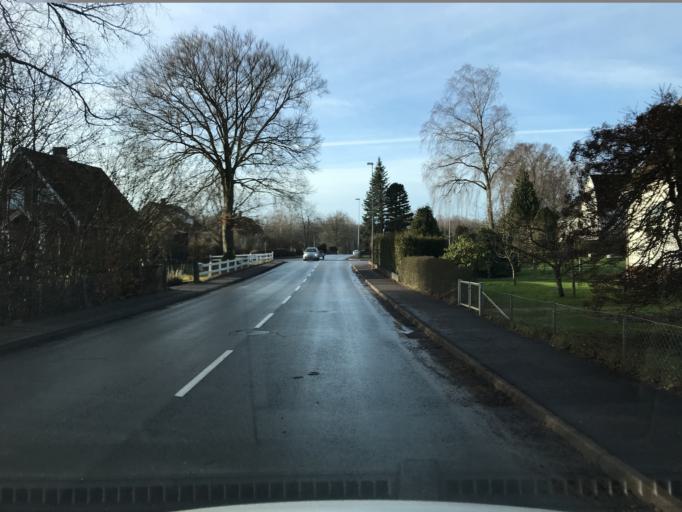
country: SE
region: Skane
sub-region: Hassleholms Kommun
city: Bjarnum
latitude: 56.2971
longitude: 13.7253
